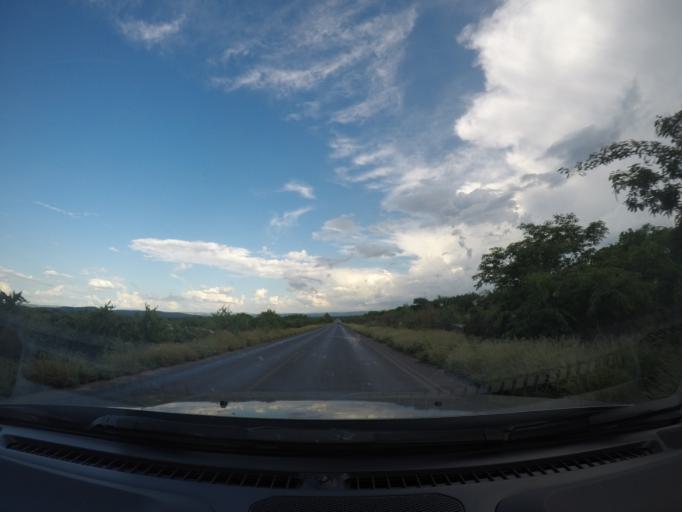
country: BR
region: Bahia
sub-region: Ibotirama
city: Ibotirama
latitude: -12.1331
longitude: -43.3356
